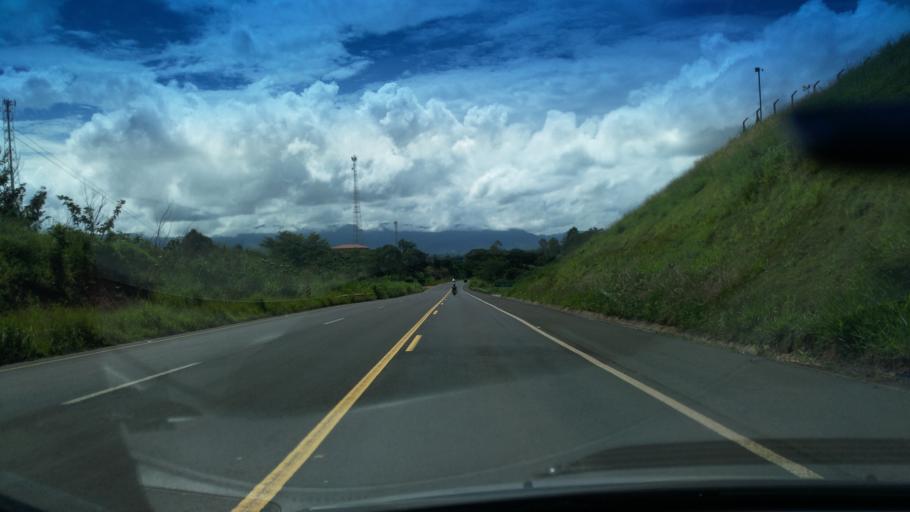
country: BR
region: Sao Paulo
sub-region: Santo Antonio Do Jardim
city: Espirito Santo do Pinhal
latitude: -22.1270
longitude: -46.6907
